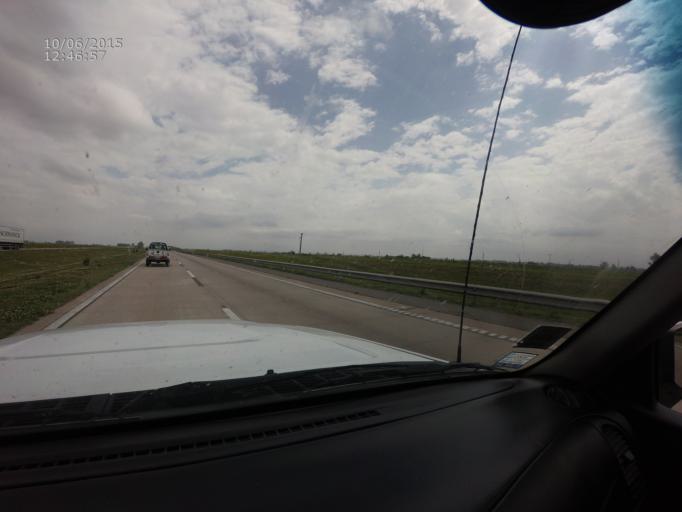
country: AR
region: Santa Fe
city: Canada de Gomez
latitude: -32.8425
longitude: -61.4176
